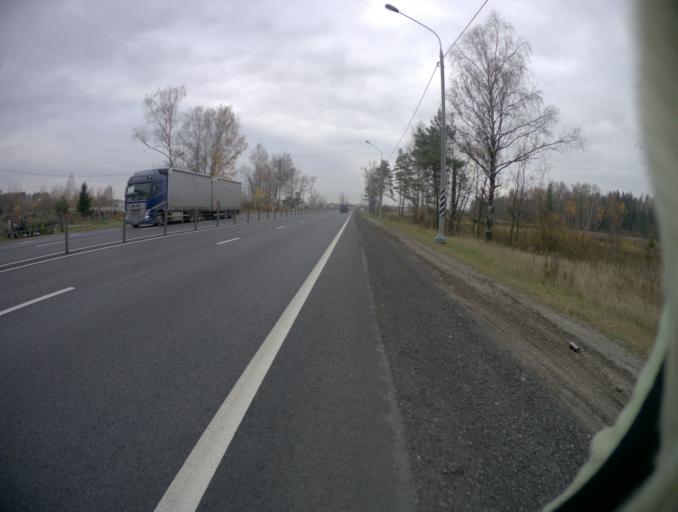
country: RU
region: Moskovskaya
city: Malaya Dubna
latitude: 55.8696
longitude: 38.9639
